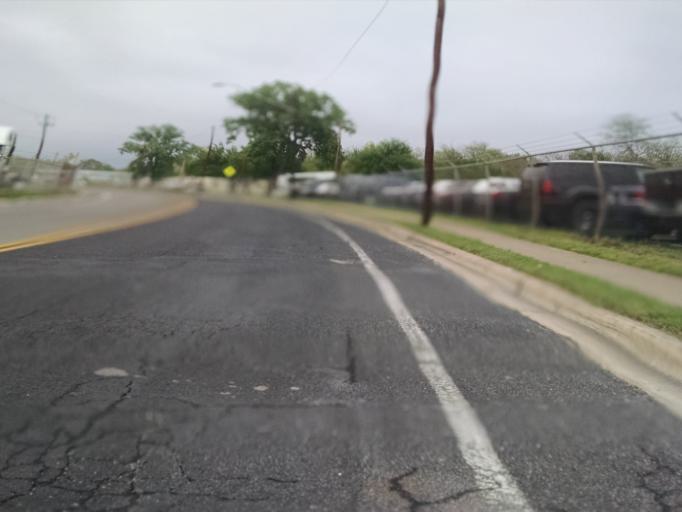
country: US
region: Texas
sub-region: Travis County
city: Austin
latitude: 30.3244
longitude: -97.7229
